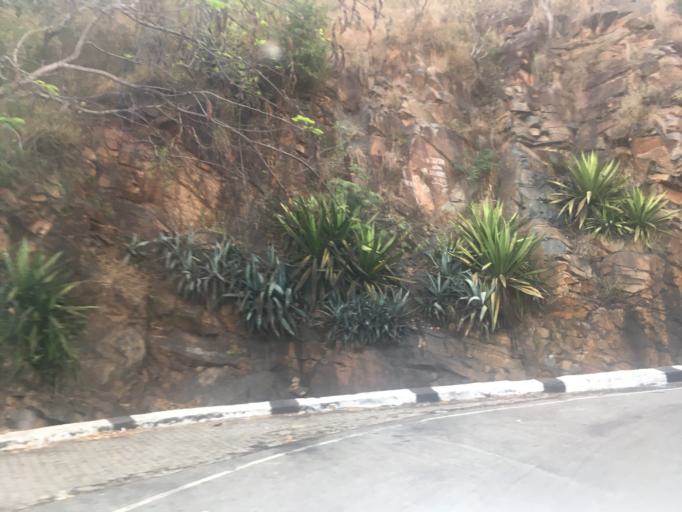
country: IN
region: Andhra Pradesh
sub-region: Chittoor
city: Tirumala
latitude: 13.6695
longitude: 79.3486
